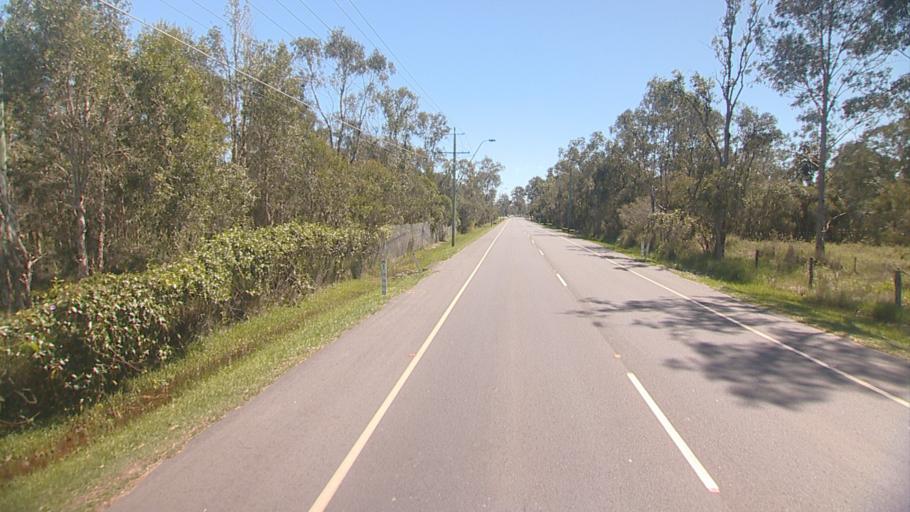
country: AU
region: Queensland
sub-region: Logan
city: Logan City
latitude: -27.6674
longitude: 153.0912
